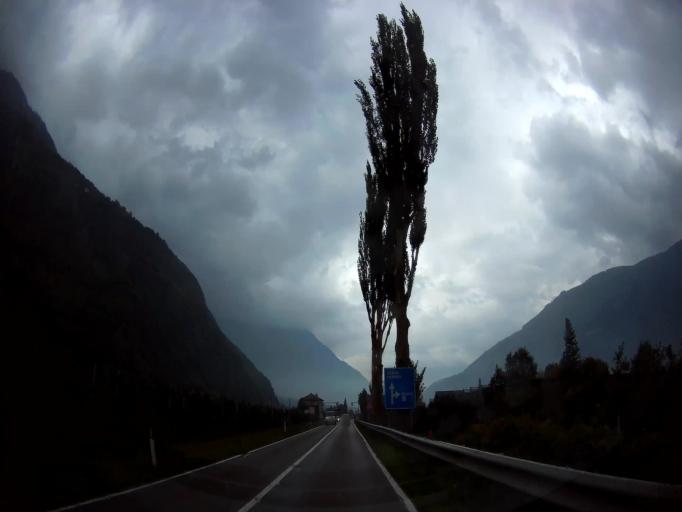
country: IT
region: Trentino-Alto Adige
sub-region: Bolzano
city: Plaus
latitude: 46.6596
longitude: 11.0349
